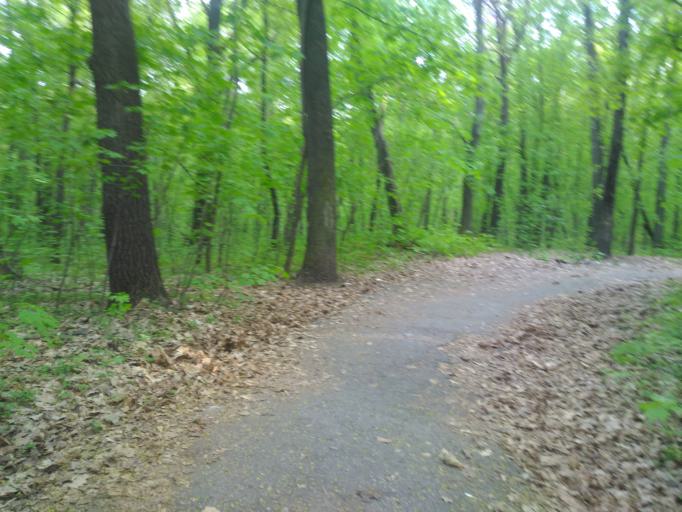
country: RU
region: Ulyanovsk
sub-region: Ulyanovskiy Rayon
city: Ulyanovsk
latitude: 54.2746
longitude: 48.3410
